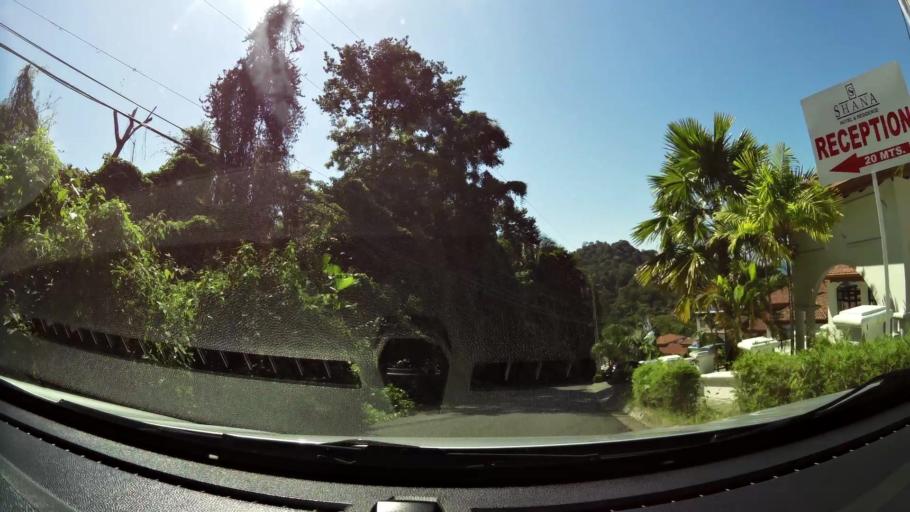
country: CR
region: Puntarenas
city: Quepos
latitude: 9.4005
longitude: -84.1644
